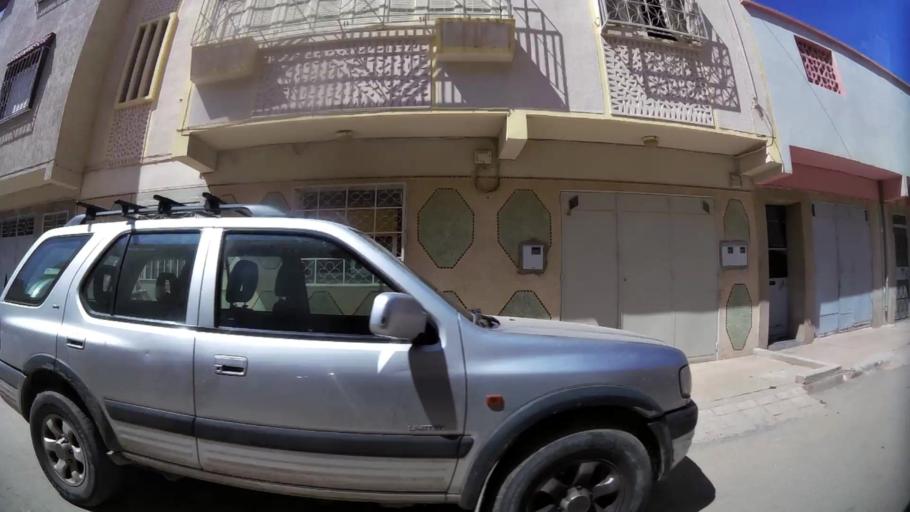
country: MA
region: Oriental
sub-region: Oujda-Angad
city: Oujda
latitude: 34.6719
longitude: -1.9382
